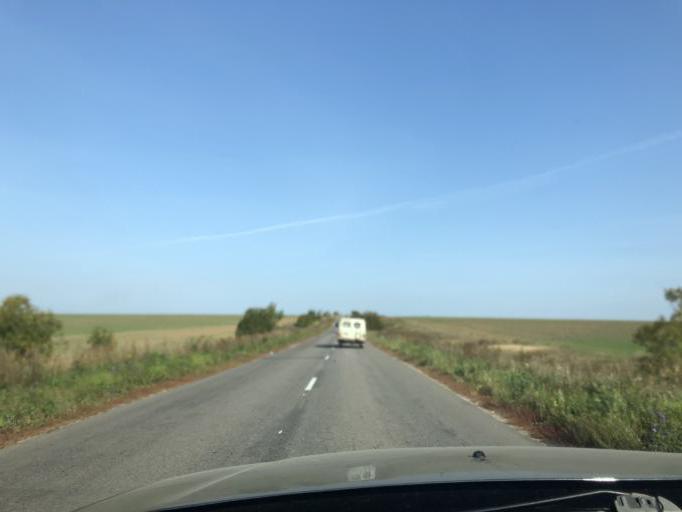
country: RU
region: Tula
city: Novogurovskiy
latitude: 54.3993
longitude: 37.3146
